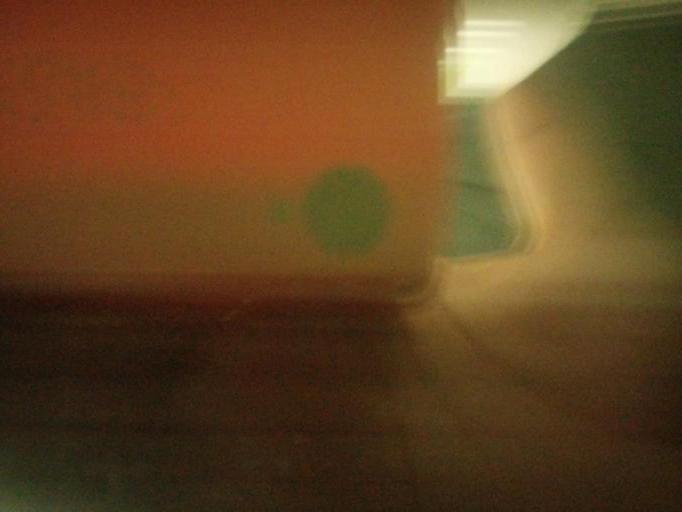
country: JP
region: Gifu
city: Tarui
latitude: 35.3612
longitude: 136.4111
